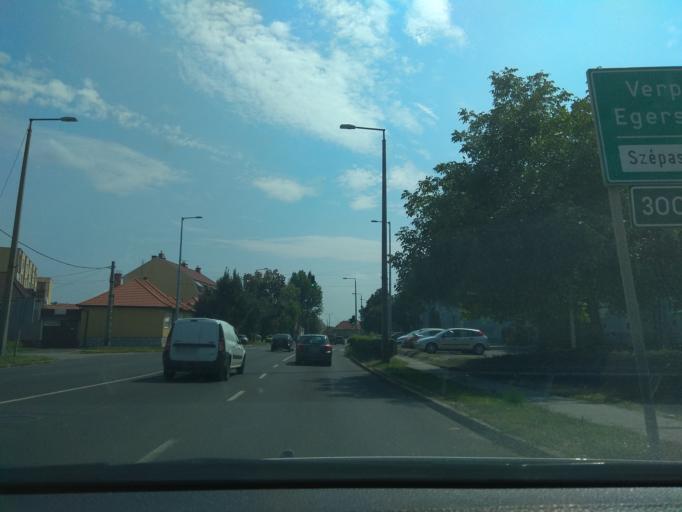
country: HU
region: Heves
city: Eger
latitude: 47.8949
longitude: 20.3693
